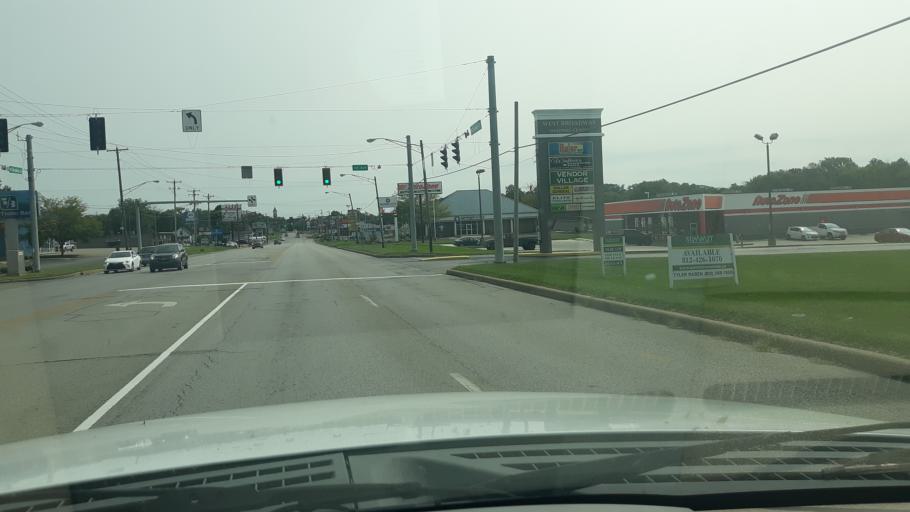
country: US
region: Indiana
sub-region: Gibson County
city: Princeton
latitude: 38.3555
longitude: -87.5863
